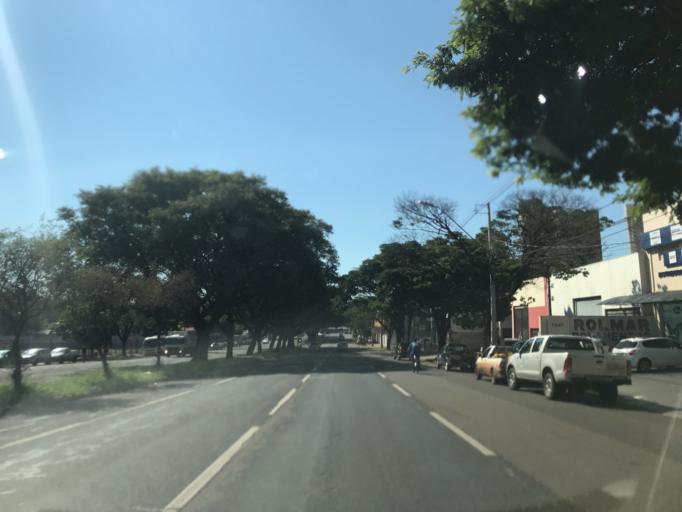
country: BR
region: Parana
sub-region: Maringa
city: Maringa
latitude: -23.4146
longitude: -51.9501
